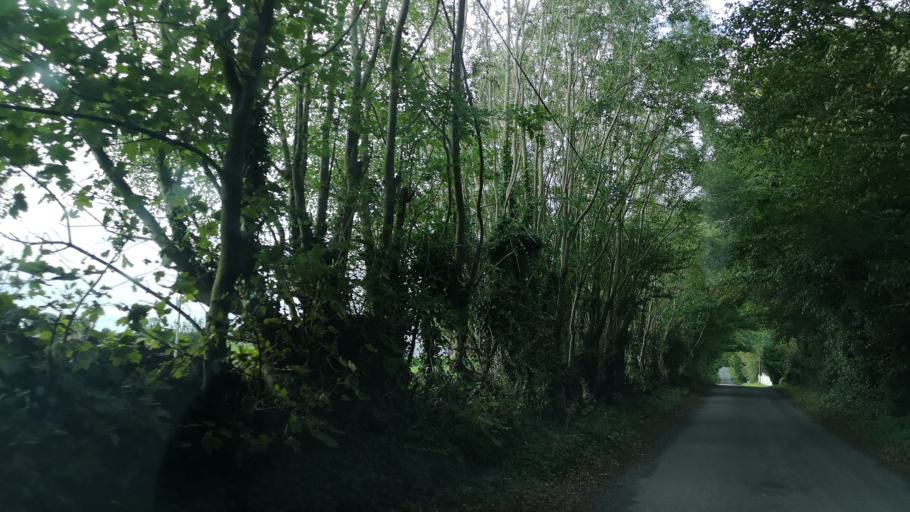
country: IE
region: Connaught
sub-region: County Galway
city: Ballinasloe
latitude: 53.3150
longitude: -8.1054
